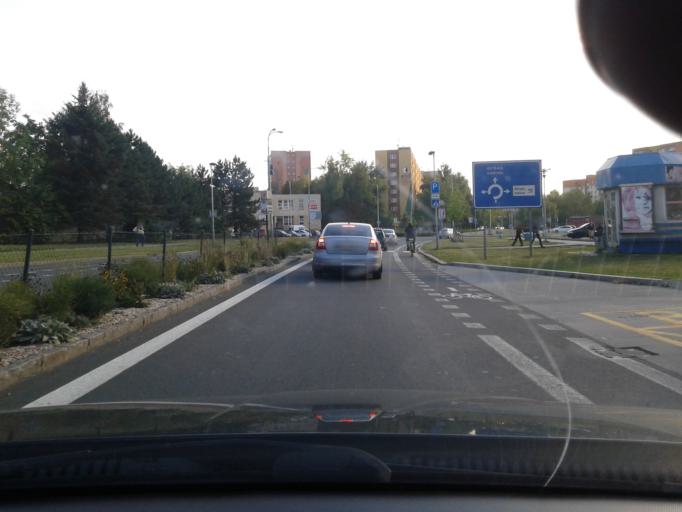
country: CZ
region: Moravskoslezsky
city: Orlova
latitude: 49.8711
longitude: 18.4254
